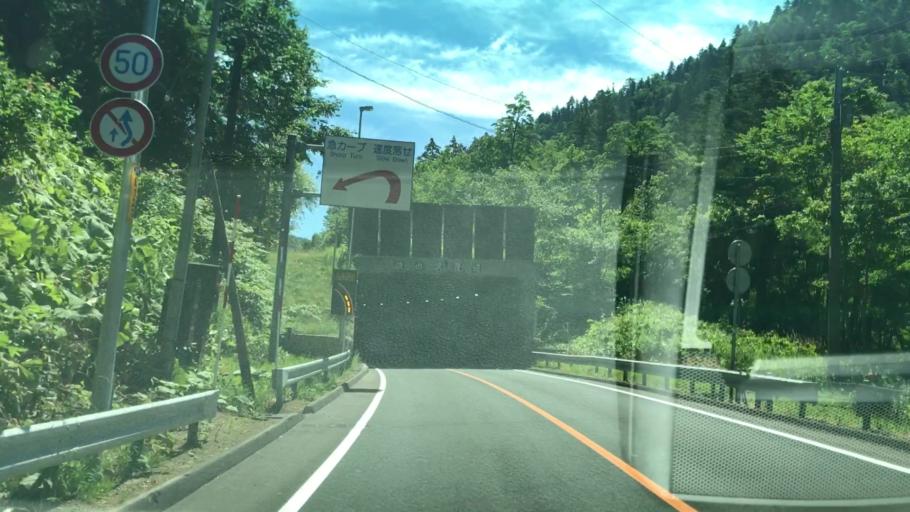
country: JP
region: Hokkaido
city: Shimo-furano
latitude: 42.9650
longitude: 142.6383
